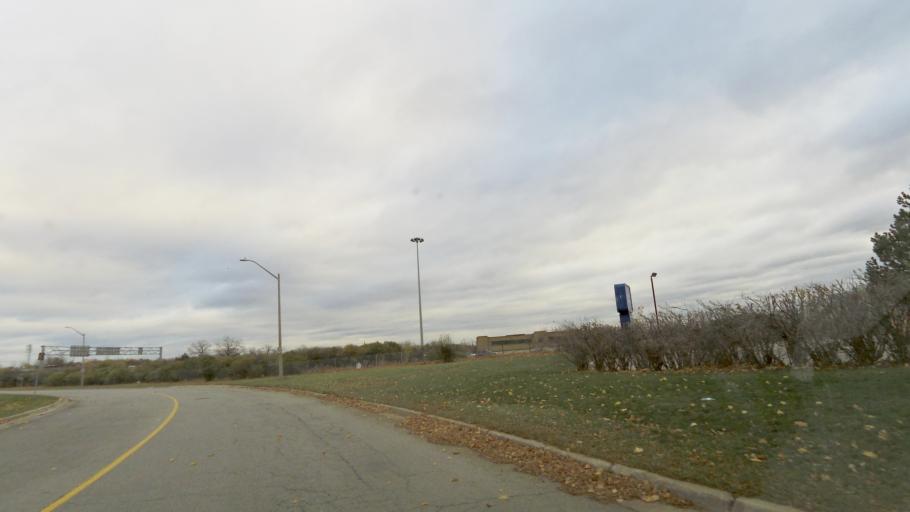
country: CA
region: Ontario
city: Oakville
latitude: 43.4645
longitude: -79.6822
